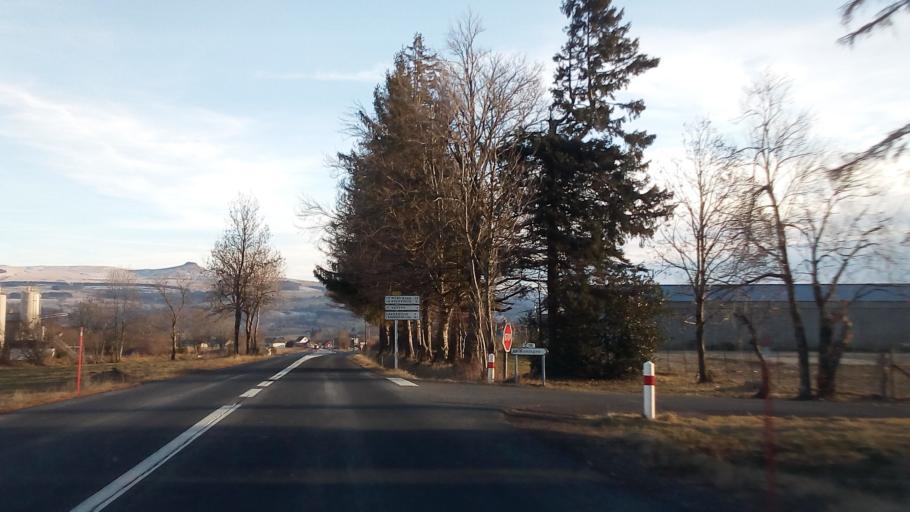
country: FR
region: Auvergne
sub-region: Departement du Puy-de-Dome
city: Saint-Sauves-d'Auvergne
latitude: 45.6530
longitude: 2.7003
